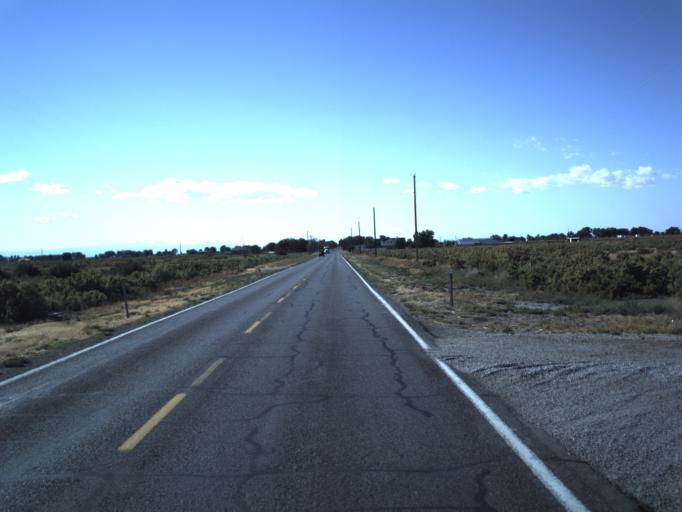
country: US
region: Utah
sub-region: Millard County
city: Delta
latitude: 39.3064
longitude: -112.6525
